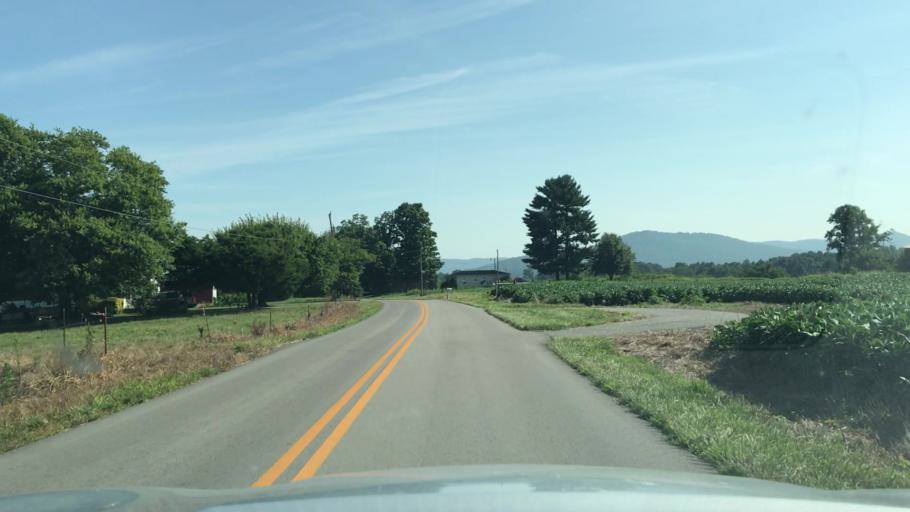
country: US
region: Kentucky
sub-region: Clinton County
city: Albany
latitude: 36.6441
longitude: -85.0804
